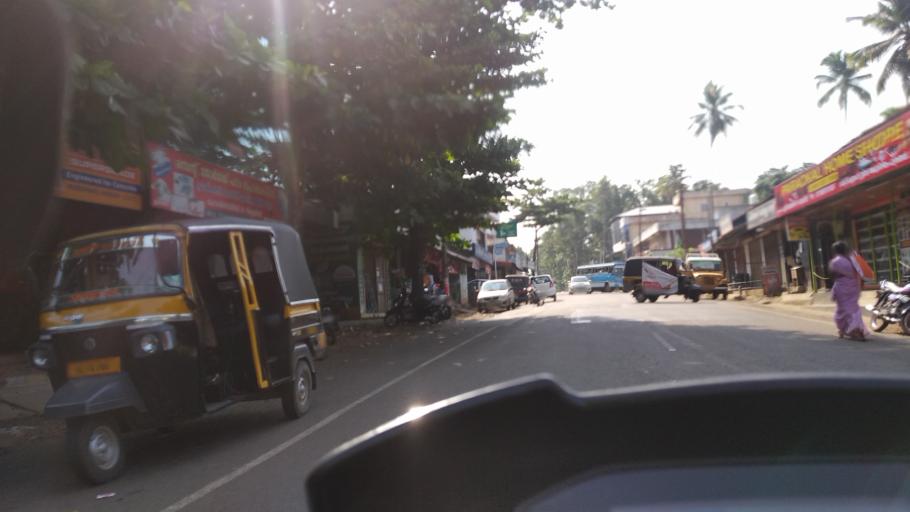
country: IN
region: Kerala
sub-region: Ernakulam
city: Piravam
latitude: 9.8305
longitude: 76.5457
